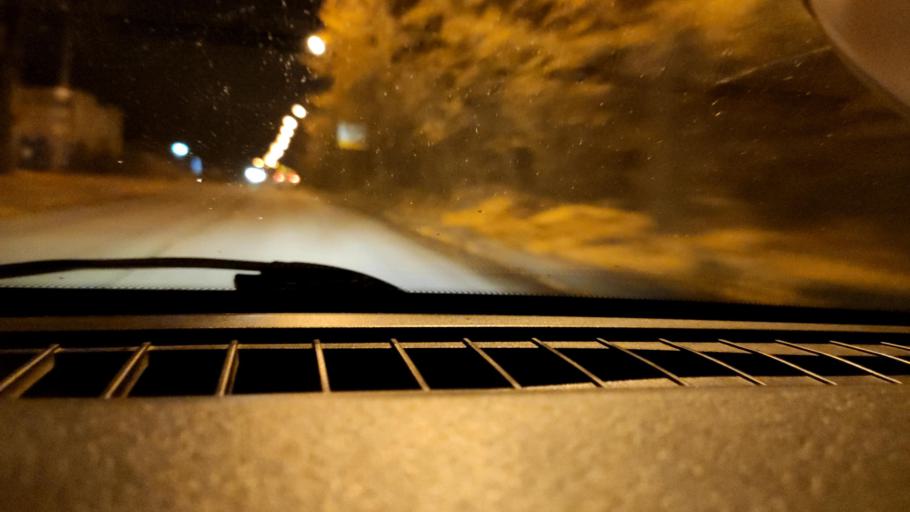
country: RU
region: Samara
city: Petra-Dubrava
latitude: 53.2383
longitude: 50.2957
